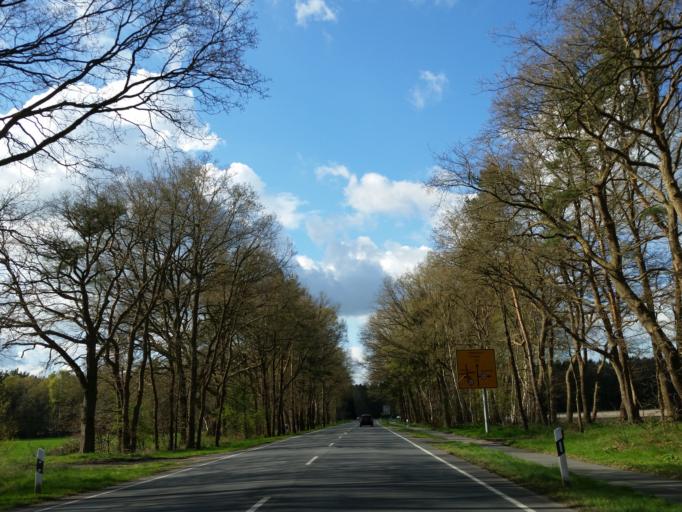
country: DE
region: Lower Saxony
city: Ahausen
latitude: 53.0621
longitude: 9.3445
